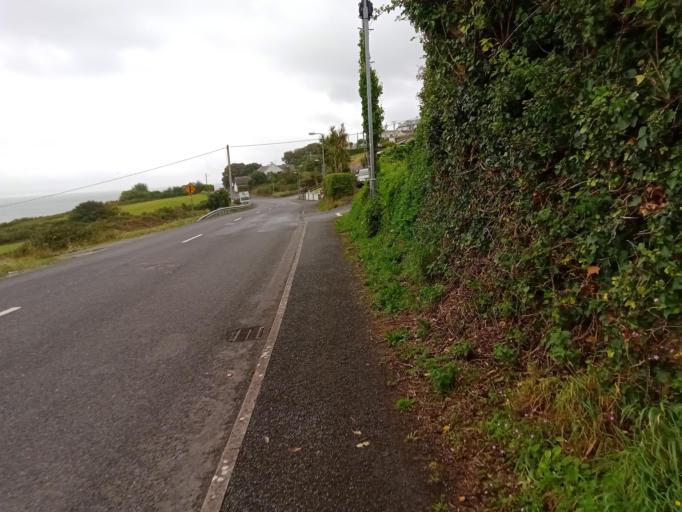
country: IE
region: Munster
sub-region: Waterford
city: Dungarvan
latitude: 52.0513
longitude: -7.5576
